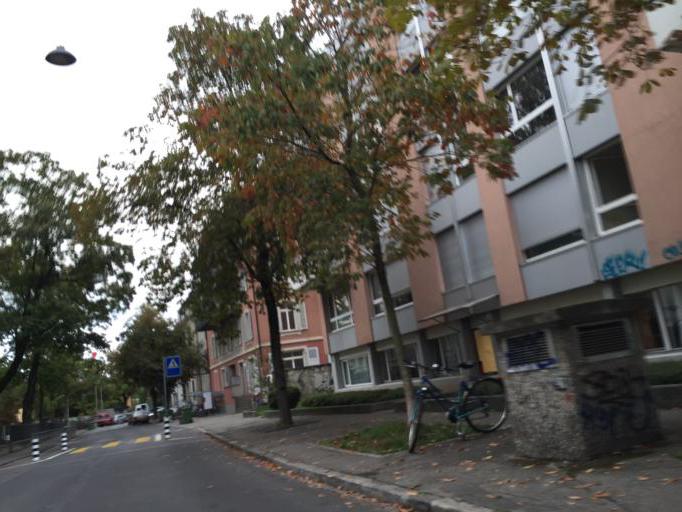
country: CH
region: Bern
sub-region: Bern-Mittelland District
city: Bern
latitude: 46.9580
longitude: 7.4447
